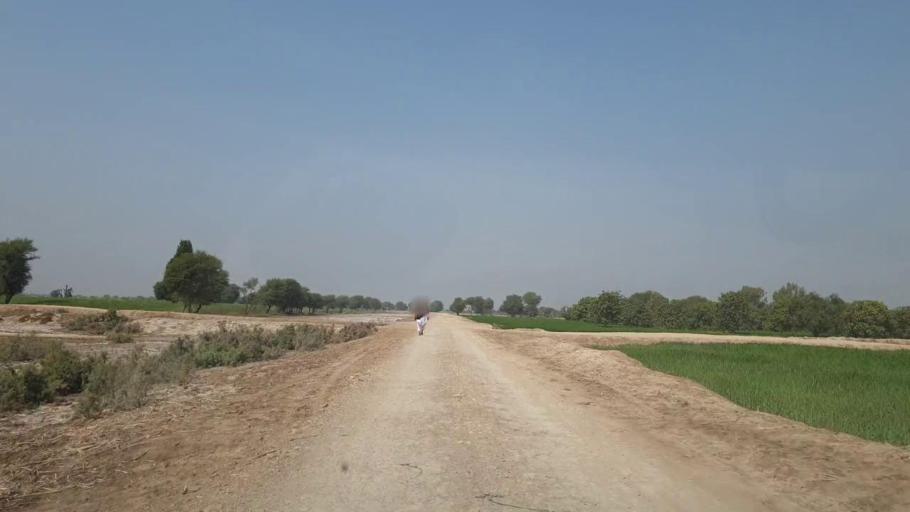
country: PK
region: Sindh
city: Mirpur Khas
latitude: 25.6548
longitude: 69.1359
